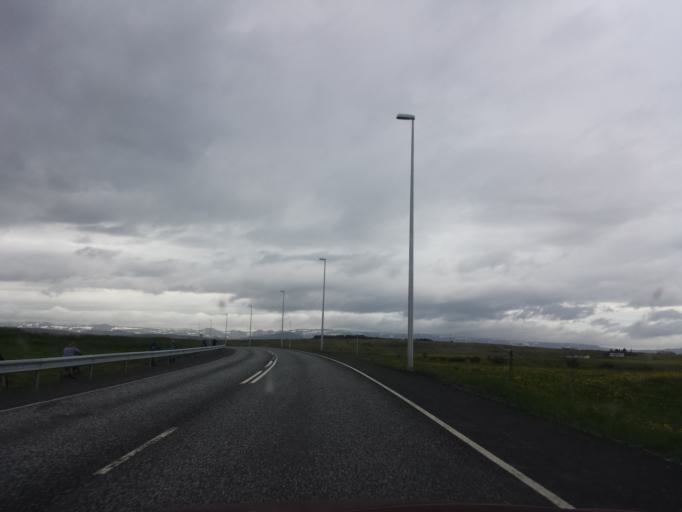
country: IS
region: Capital Region
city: Alftanes
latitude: 64.0980
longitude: -22.0053
